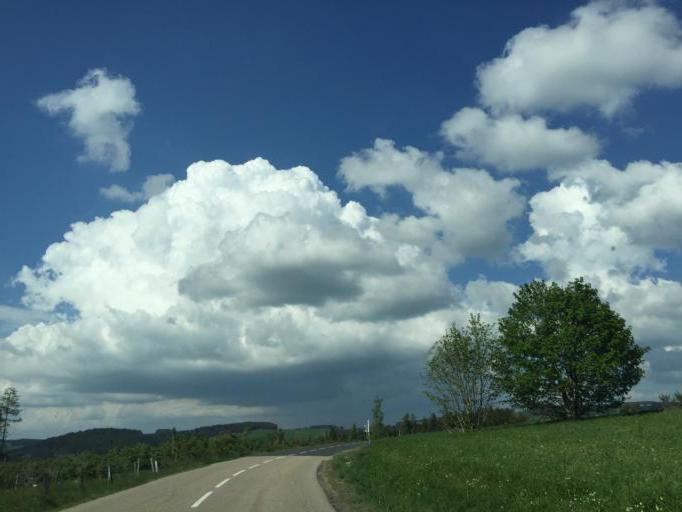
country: FR
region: Rhone-Alpes
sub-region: Departement de la Loire
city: Saint-Genest-Malifaux
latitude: 45.3556
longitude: 4.4661
